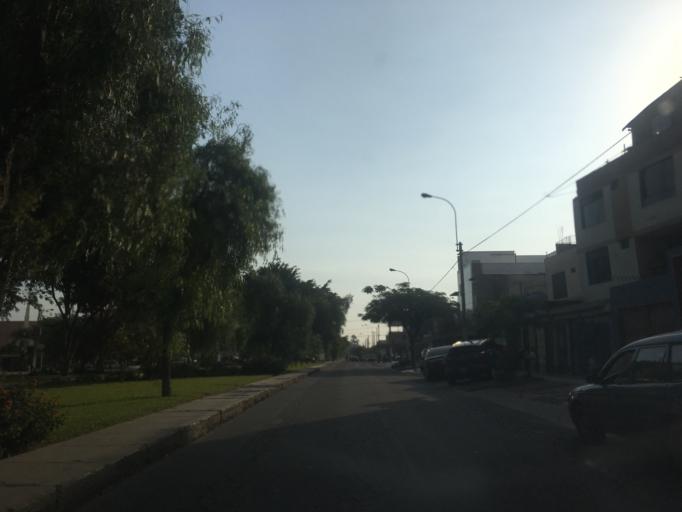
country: PE
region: Lima
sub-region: Lima
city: La Molina
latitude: -12.0683
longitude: -76.9476
